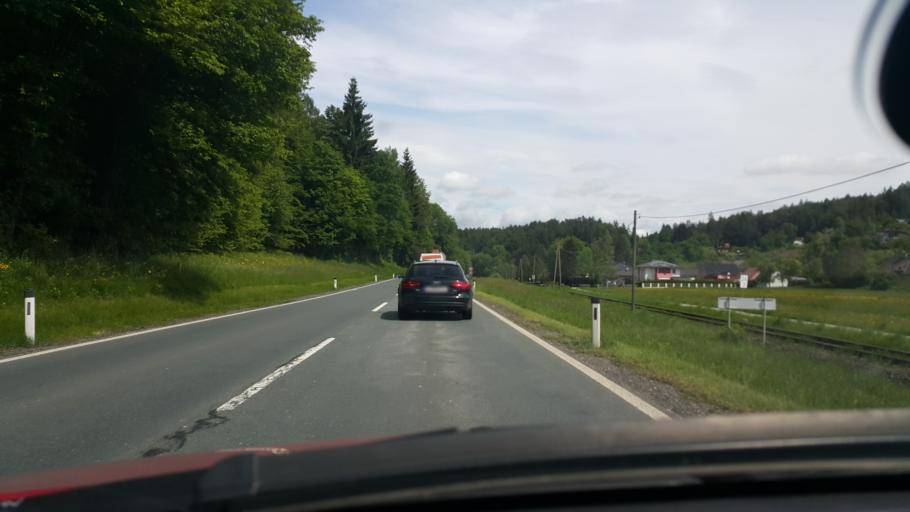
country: AT
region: Carinthia
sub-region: Politischer Bezirk Klagenfurt Land
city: Maria Rain
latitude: 46.5699
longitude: 14.2856
